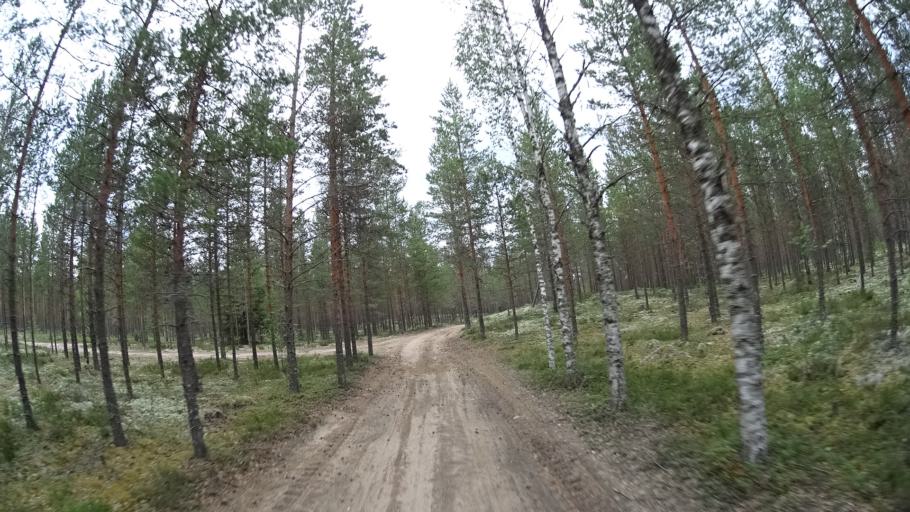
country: FI
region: Satakunta
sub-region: Pohjois-Satakunta
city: Jaemijaervi
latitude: 61.7606
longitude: 22.7844
